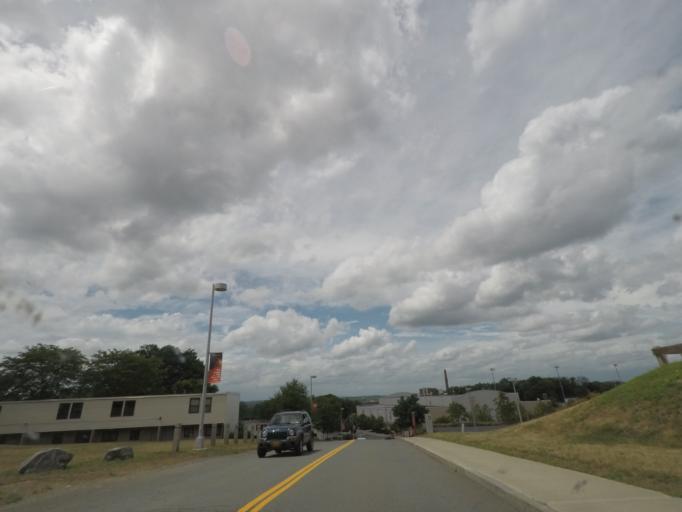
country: US
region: New York
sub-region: Rensselaer County
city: Troy
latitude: 42.7310
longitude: -73.6675
